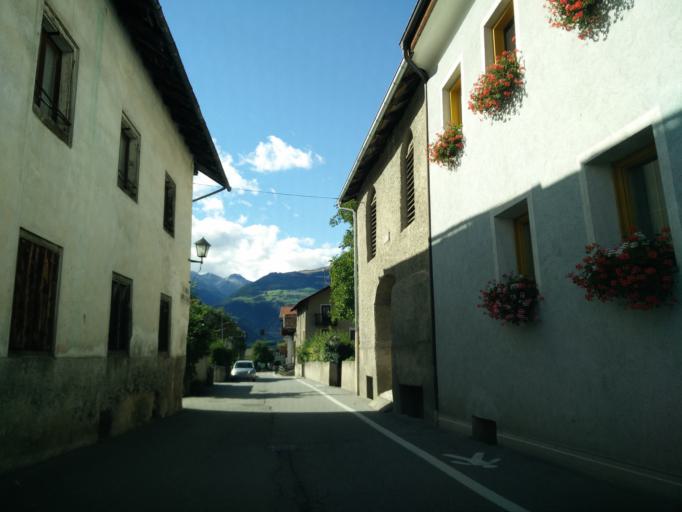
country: IT
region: Trentino-Alto Adige
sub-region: Bolzano
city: Sluderno
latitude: 46.6655
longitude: 10.5834
